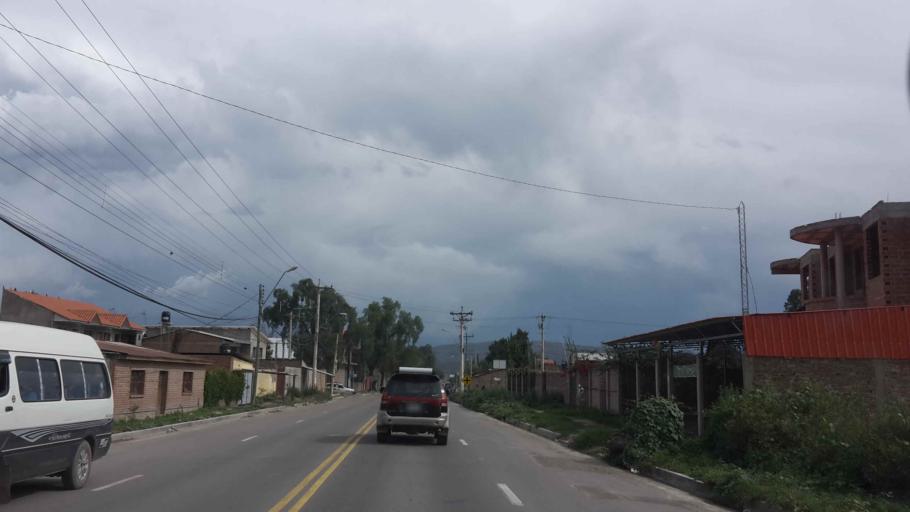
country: BO
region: Cochabamba
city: Cochabamba
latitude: -17.3725
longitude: -66.2522
